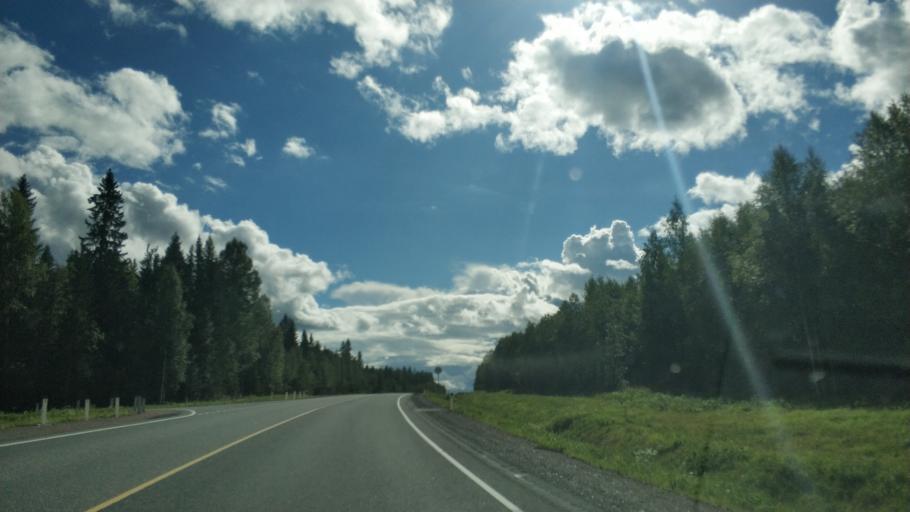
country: RU
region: Republic of Karelia
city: Ruskeala
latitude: 61.8673
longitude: 30.6540
